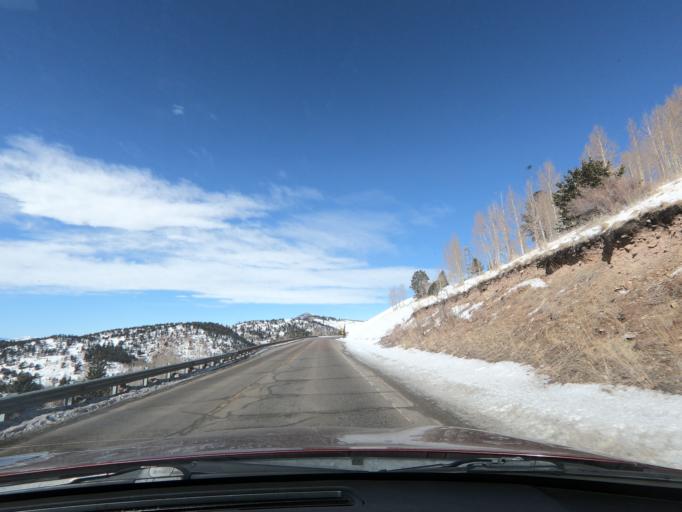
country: US
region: Colorado
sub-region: Teller County
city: Cripple Creek
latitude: 38.7236
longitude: -105.1663
